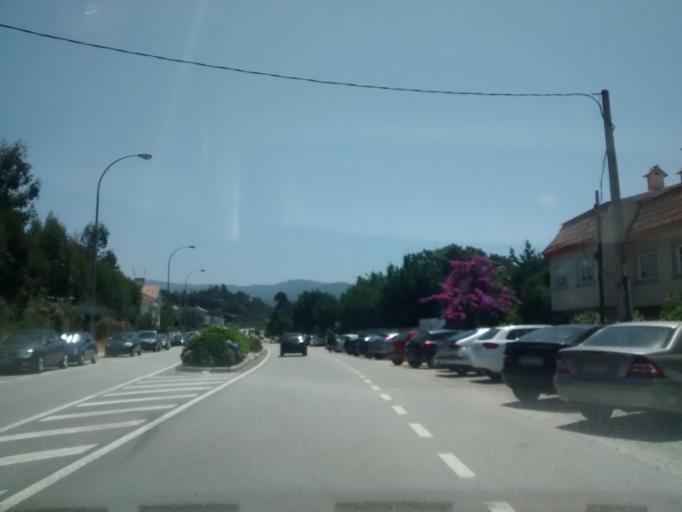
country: ES
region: Galicia
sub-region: Provincia de Pontevedra
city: Nigran
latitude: 42.1229
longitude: -8.8190
